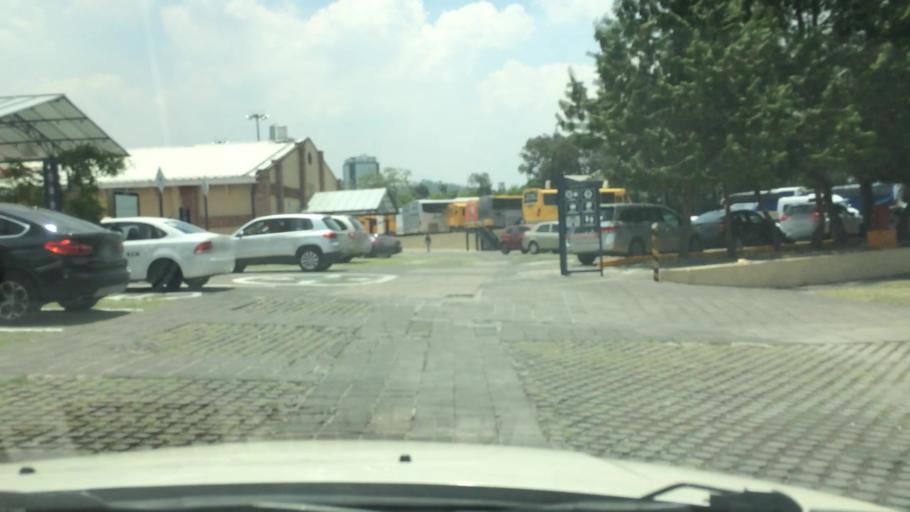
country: MX
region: Mexico City
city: Tlalpan
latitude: 19.2988
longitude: -99.1808
